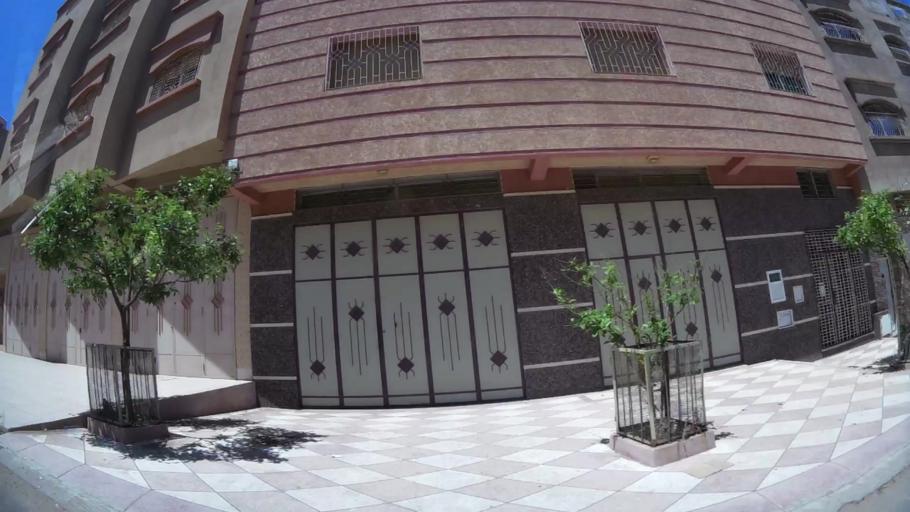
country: MA
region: Oriental
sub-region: Oujda-Angad
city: Oujda
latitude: 34.6808
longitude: -1.9436
